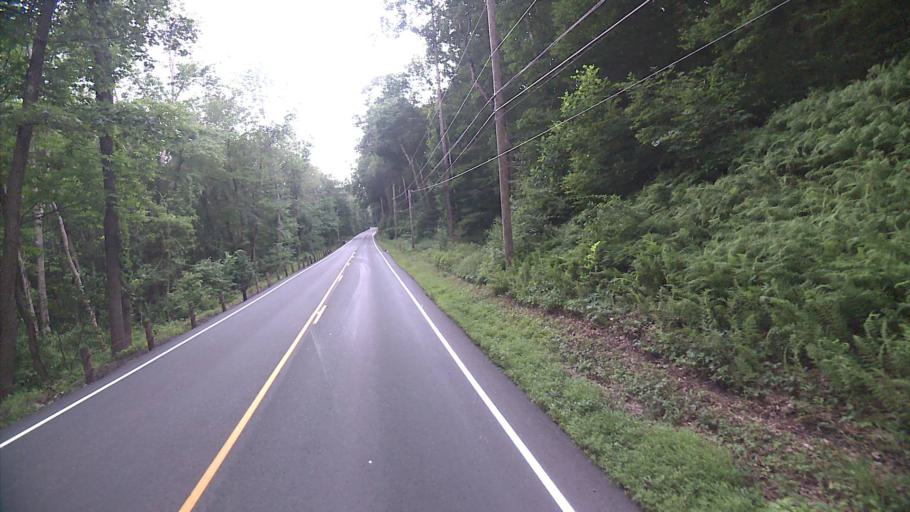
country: US
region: Connecticut
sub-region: New Haven County
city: Heritage Village
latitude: 41.5269
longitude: -73.2708
